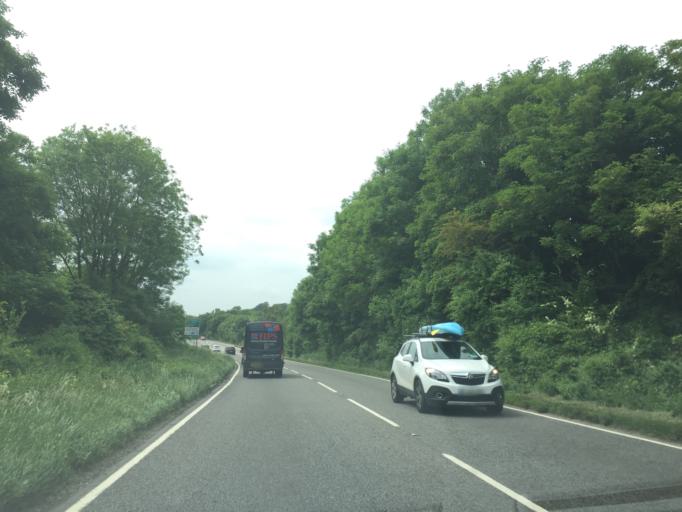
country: GB
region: England
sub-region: Hampshire
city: Kings Worthy
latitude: 51.0601
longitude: -1.2869
